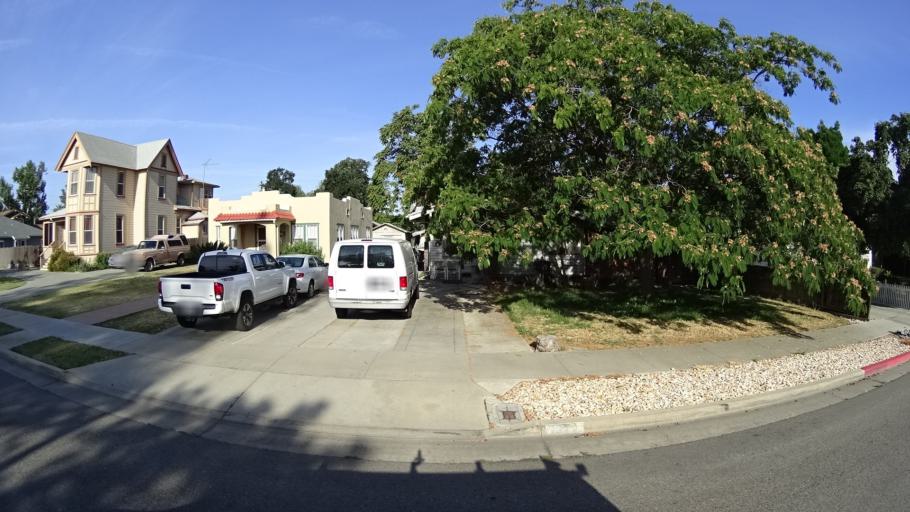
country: US
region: California
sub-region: Kings County
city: Hanford
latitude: 36.3395
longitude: -119.6461
